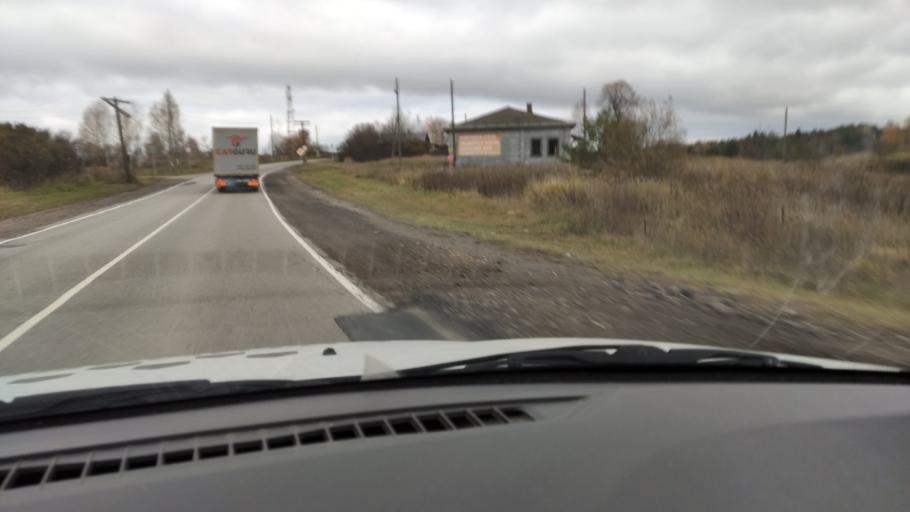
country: RU
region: Kirov
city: Belaya Kholunitsa
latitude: 58.8036
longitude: 50.5405
